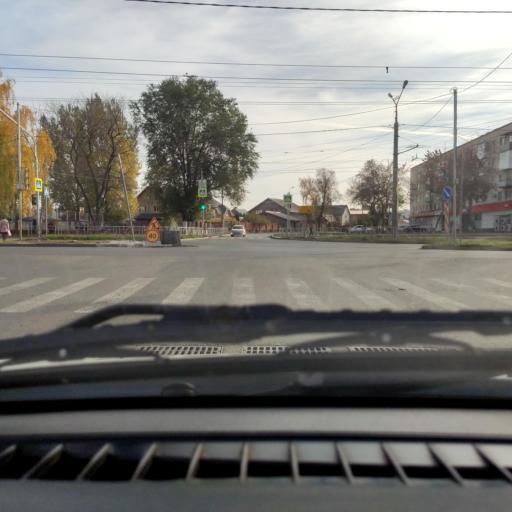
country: RU
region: Samara
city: Tol'yatti
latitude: 53.5316
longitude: 49.4185
